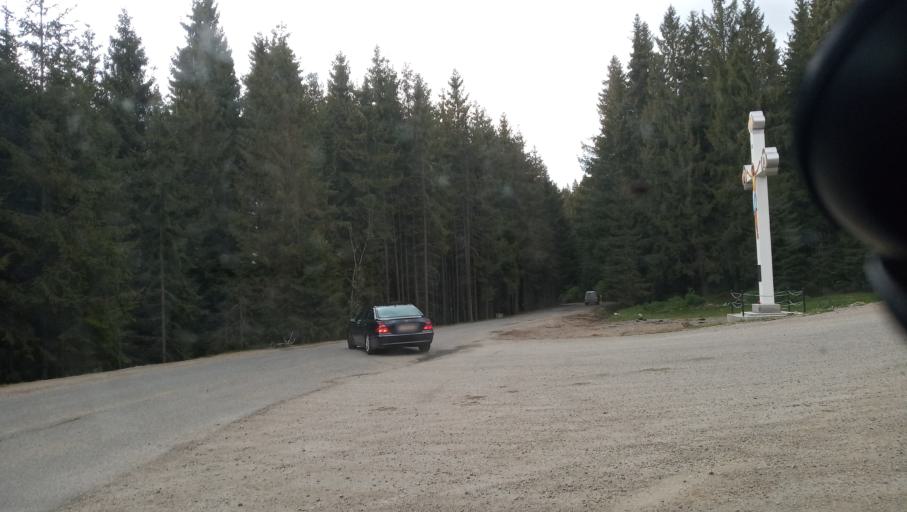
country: RO
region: Cluj
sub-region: Comuna Belis
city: Belis
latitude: 46.6517
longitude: 23.0397
